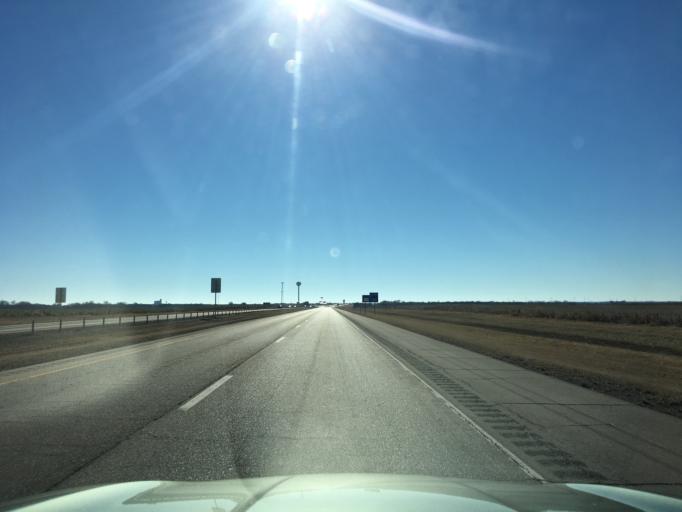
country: US
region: Oklahoma
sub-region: Kay County
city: Blackwell
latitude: 36.9555
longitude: -97.3458
